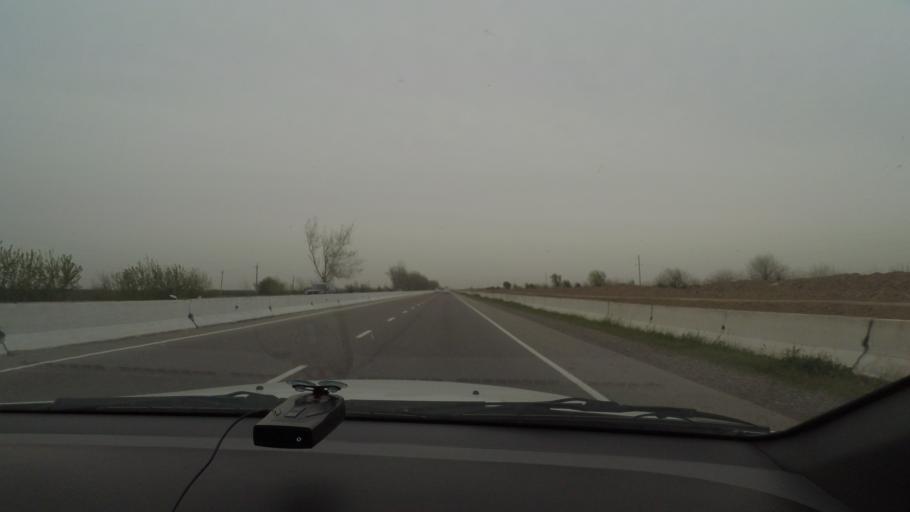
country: UZ
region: Jizzax
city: Dustlik
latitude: 40.4068
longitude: 68.1972
